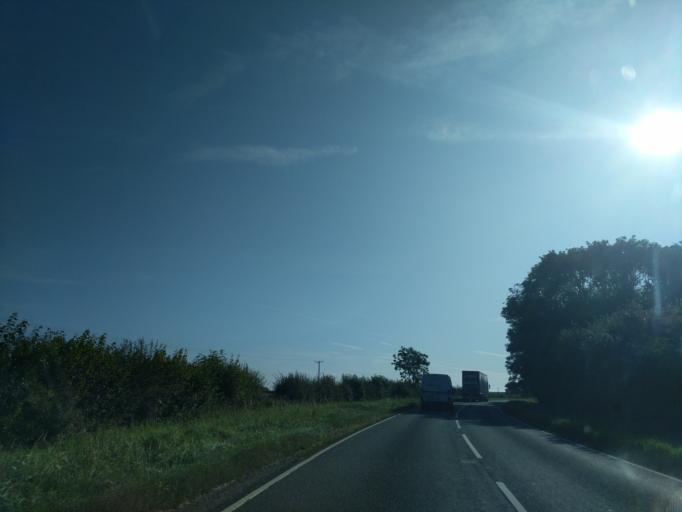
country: GB
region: England
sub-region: District of Rutland
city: Clipsham
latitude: 52.8040
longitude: -0.6006
